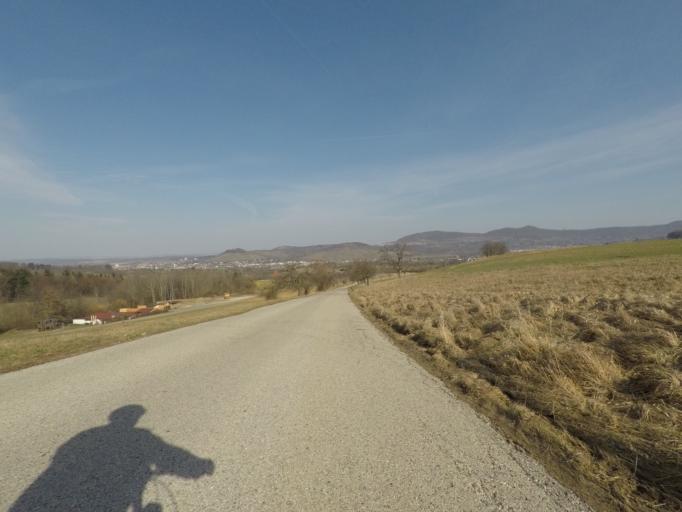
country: DE
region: Baden-Wuerttemberg
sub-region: Tuebingen Region
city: Metzingen
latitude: 48.5114
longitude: 9.2939
